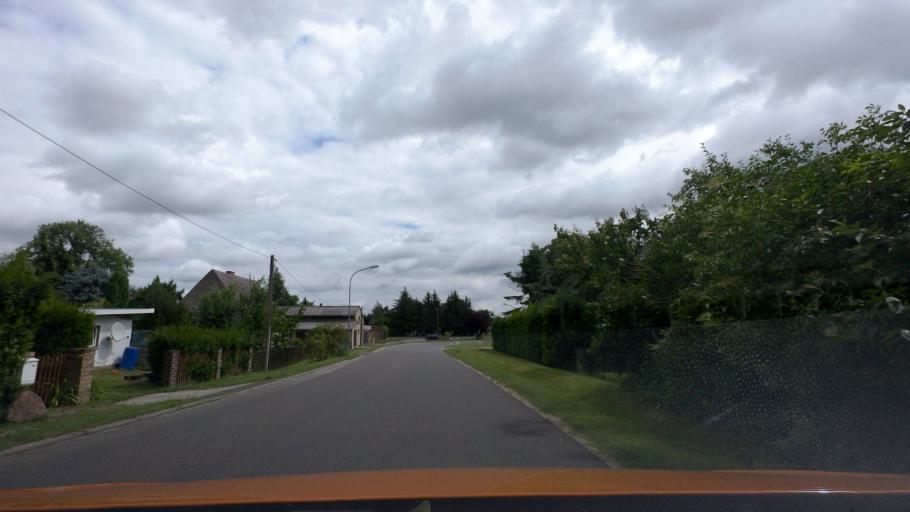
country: DE
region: Brandenburg
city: Bliesdorf
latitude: 52.6891
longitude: 14.1405
